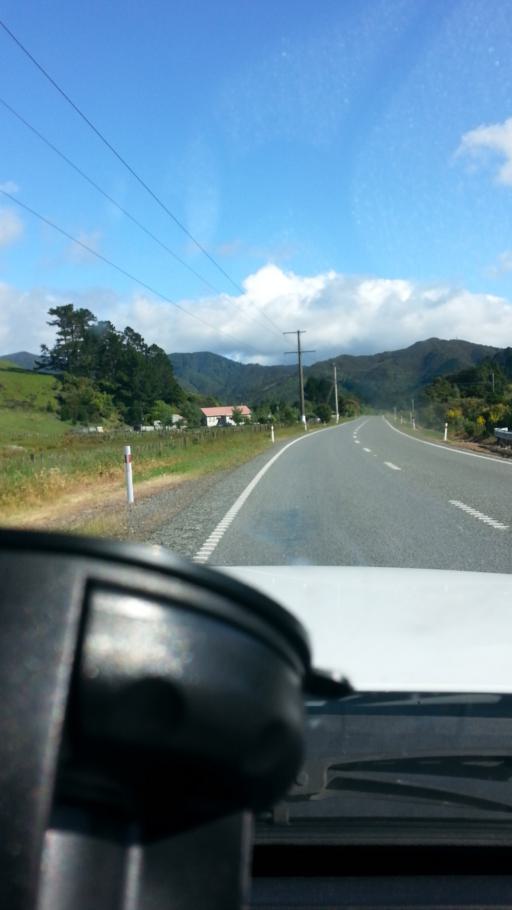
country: NZ
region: Wellington
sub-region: Masterton District
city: Masterton
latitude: -40.7702
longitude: 175.6097
